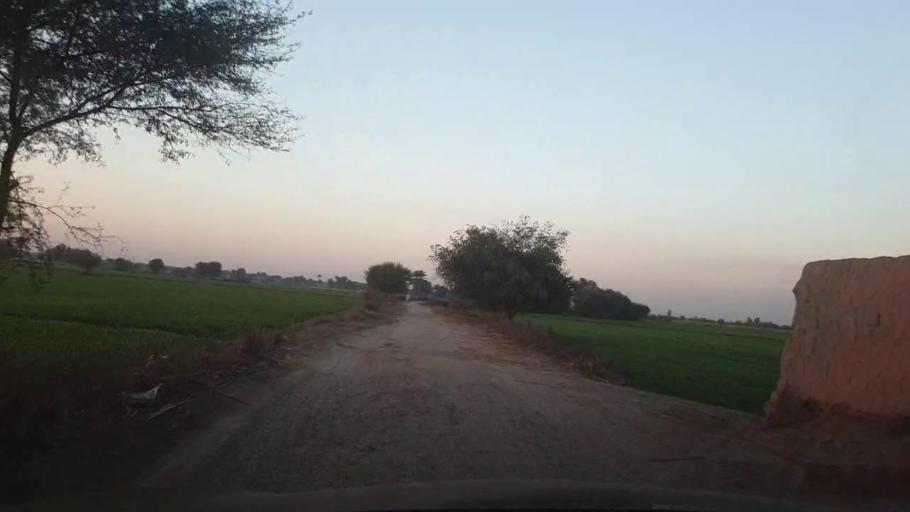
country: PK
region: Sindh
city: Ubauro
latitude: 28.1690
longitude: 69.6355
